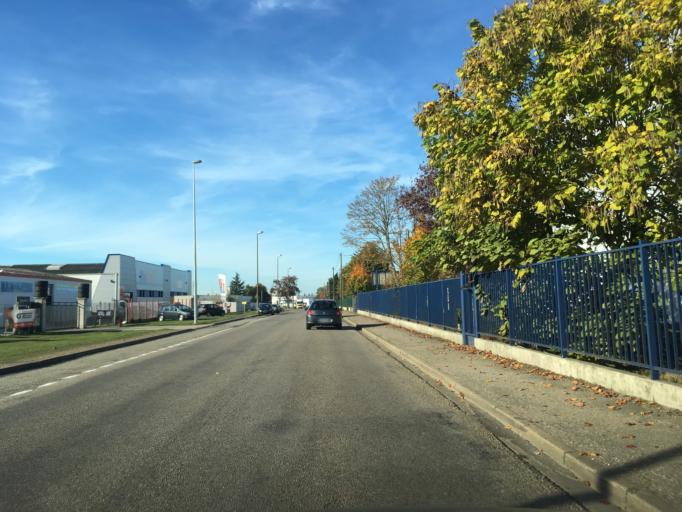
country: FR
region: Haute-Normandie
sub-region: Departement de l'Eure
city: Evreux
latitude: 49.0177
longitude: 1.1852
